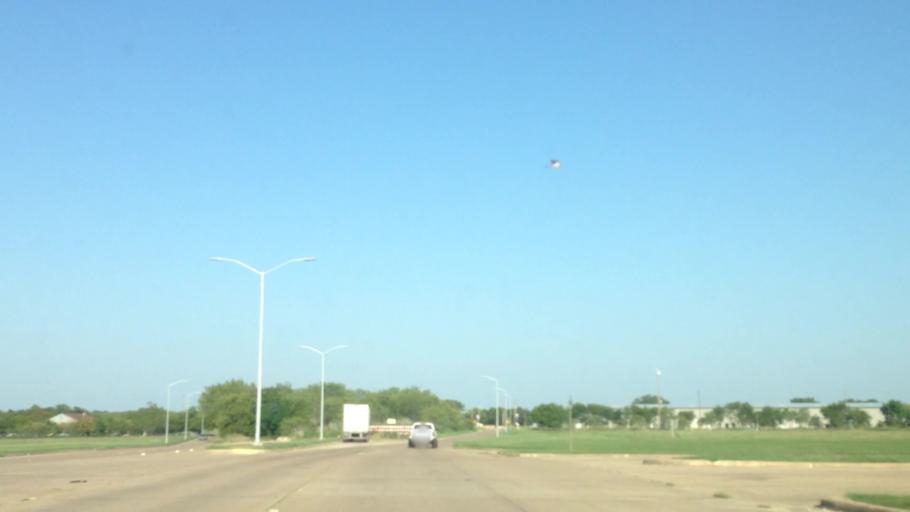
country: US
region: Texas
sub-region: Tarrant County
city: Haltom City
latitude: 32.8097
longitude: -97.3018
